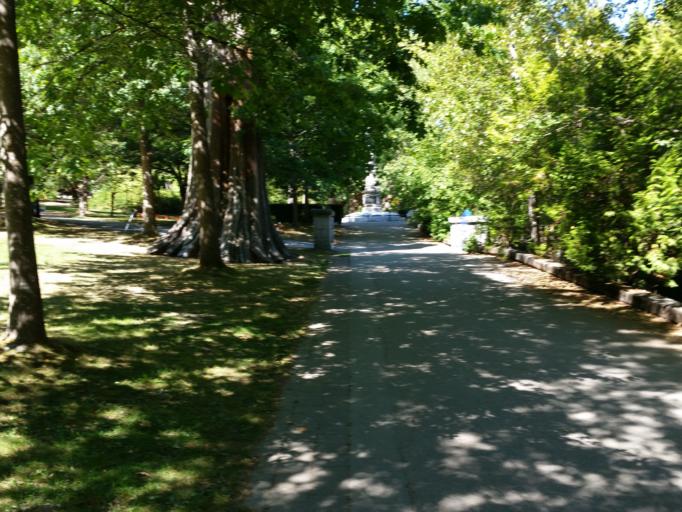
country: CA
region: British Columbia
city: West End
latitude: 49.3005
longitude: -123.1321
